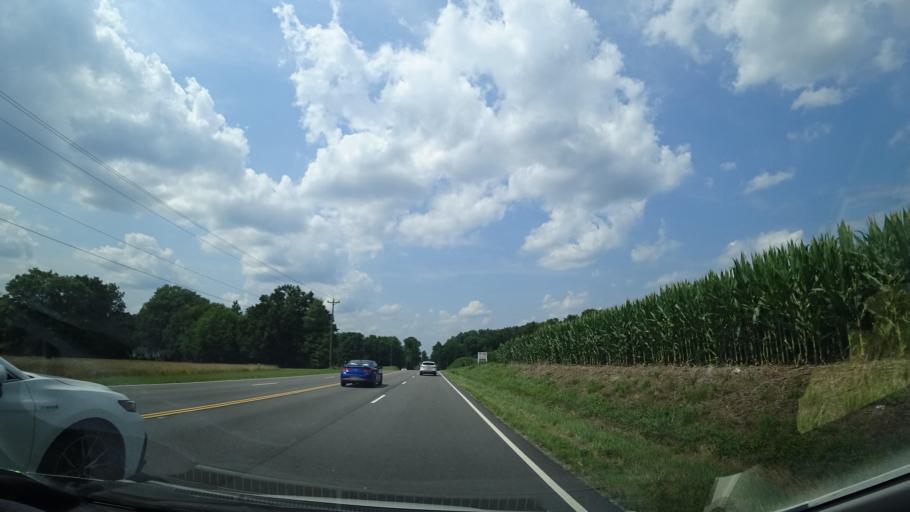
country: US
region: Virginia
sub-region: Hanover County
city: Ashland
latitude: 37.8693
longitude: -77.4642
